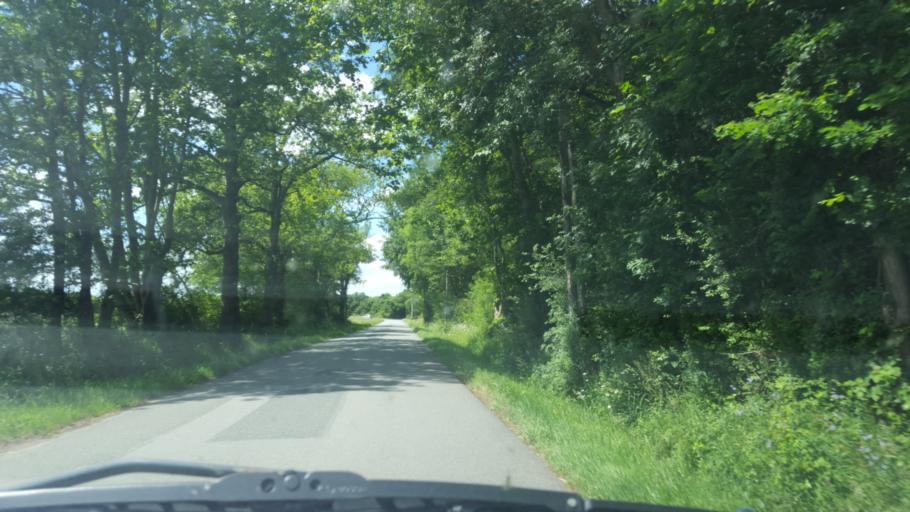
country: FR
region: Pays de la Loire
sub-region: Departement de la Loire-Atlantique
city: Saint-Philbert-de-Grand-Lieu
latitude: 47.0322
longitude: -1.6118
